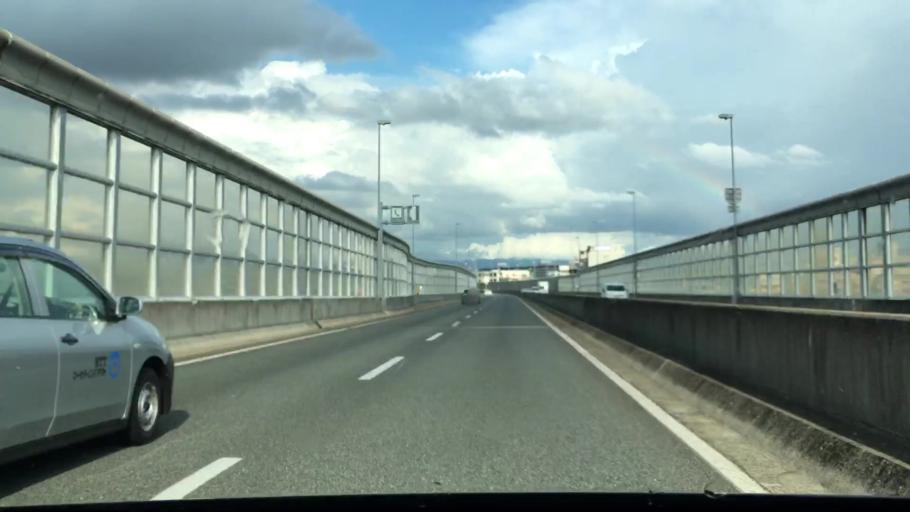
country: JP
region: Fukuoka
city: Fukuoka-shi
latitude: 33.5783
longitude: 130.3214
